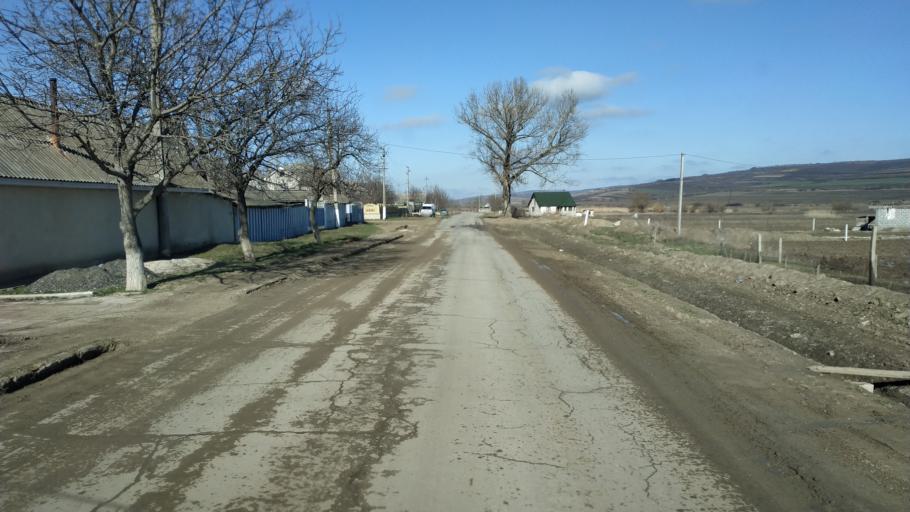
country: MD
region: Hincesti
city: Hincesti
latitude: 46.9357
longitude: 28.6387
